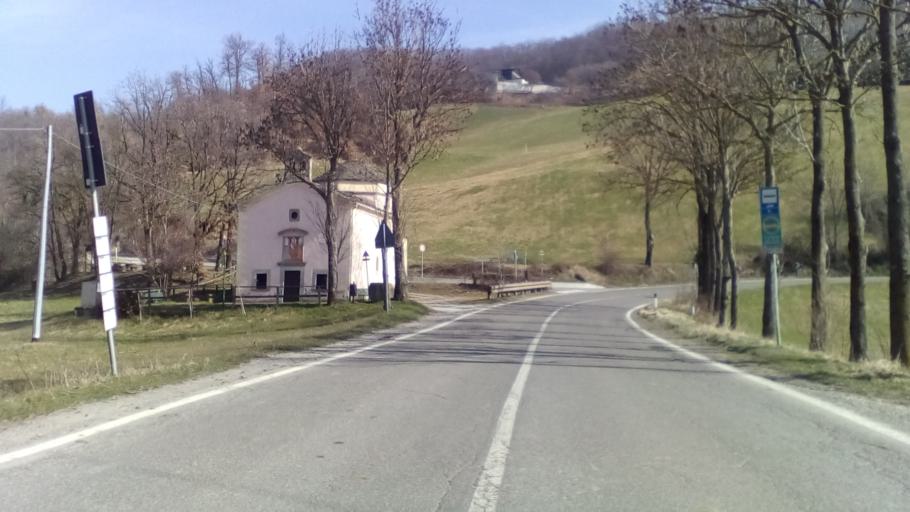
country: IT
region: Emilia-Romagna
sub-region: Provincia di Modena
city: Pavullo nel Frignano
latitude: 44.3171
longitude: 10.8098
